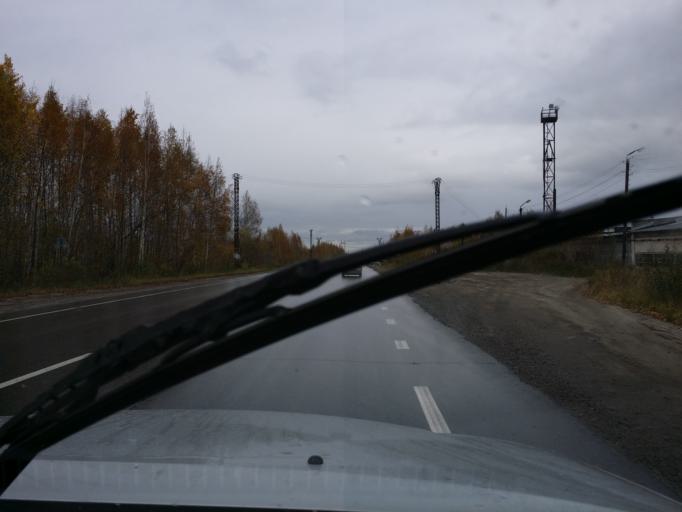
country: RU
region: Khanty-Mansiyskiy Avtonomnyy Okrug
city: Megion
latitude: 61.0723
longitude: 76.1164
